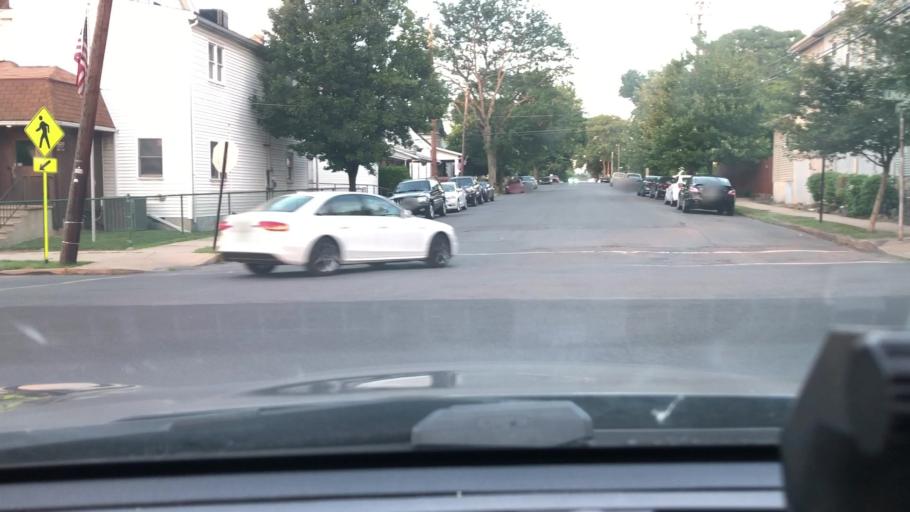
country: US
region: Pennsylvania
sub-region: Northampton County
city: Bethlehem
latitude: 40.6275
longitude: -75.3705
